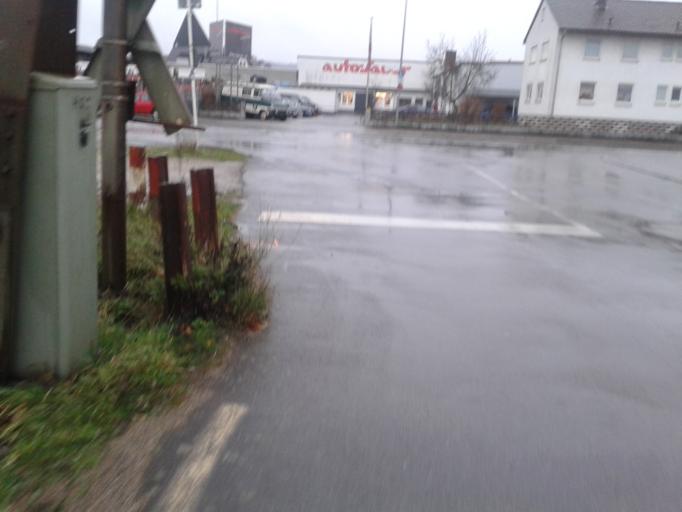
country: DE
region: Bavaria
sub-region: Upper Franconia
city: Hallstadt
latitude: 49.9126
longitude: 10.8842
